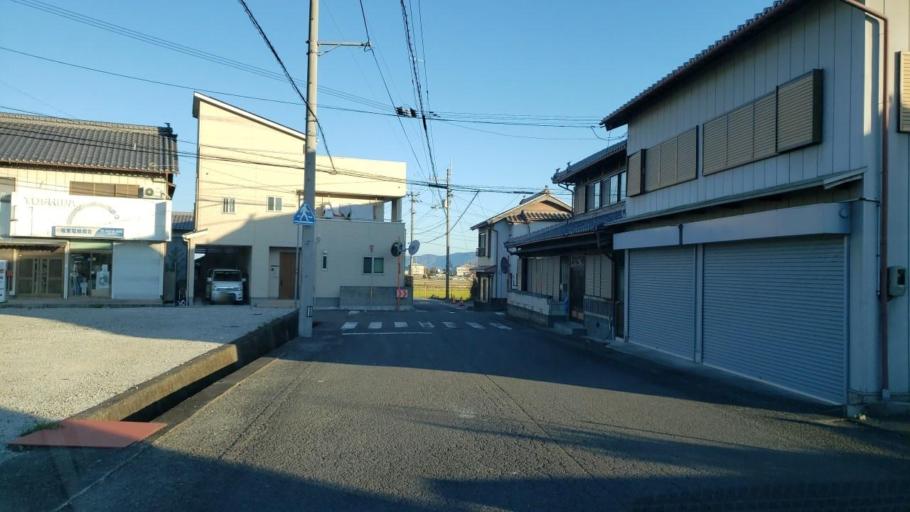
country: JP
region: Tokushima
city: Kamojimacho-jogejima
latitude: 34.0910
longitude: 134.2546
